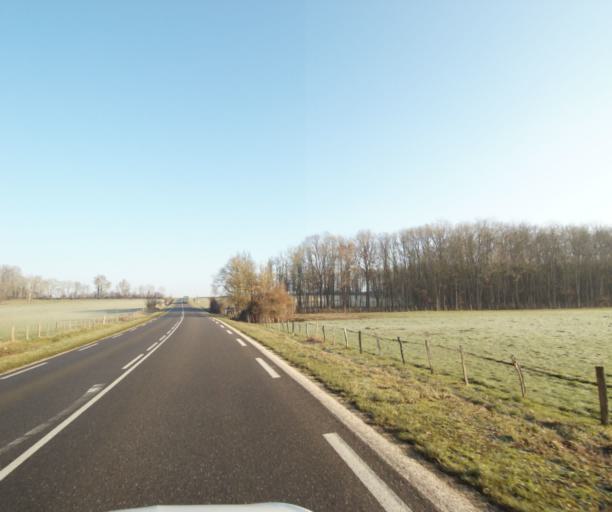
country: FR
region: Champagne-Ardenne
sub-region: Departement de la Haute-Marne
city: Montier-en-Der
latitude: 48.4499
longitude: 4.7389
